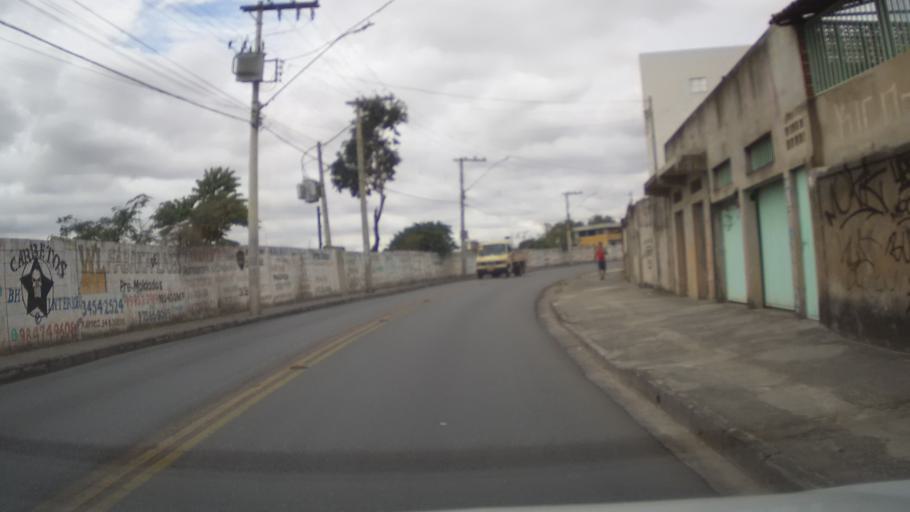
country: BR
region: Minas Gerais
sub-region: Santa Luzia
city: Santa Luzia
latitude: -19.8136
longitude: -43.9470
